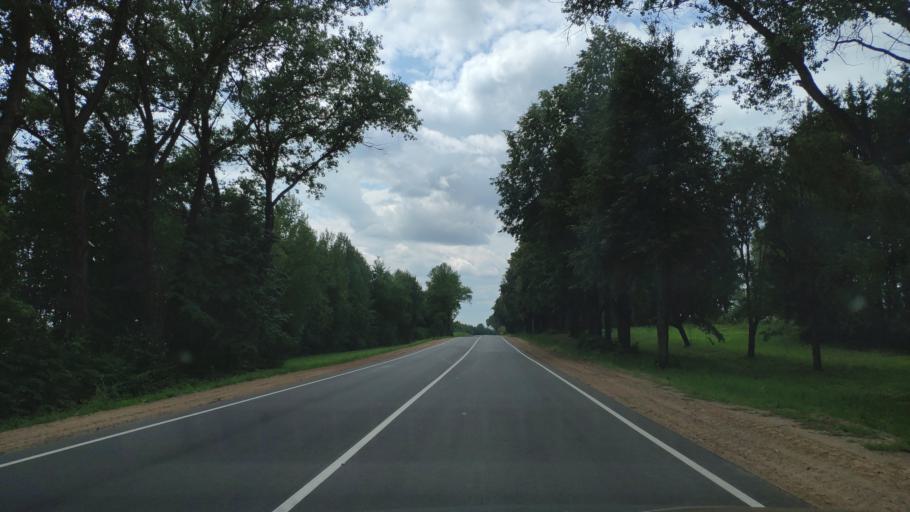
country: BY
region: Minsk
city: Syomkava
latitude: 54.0069
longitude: 27.3722
